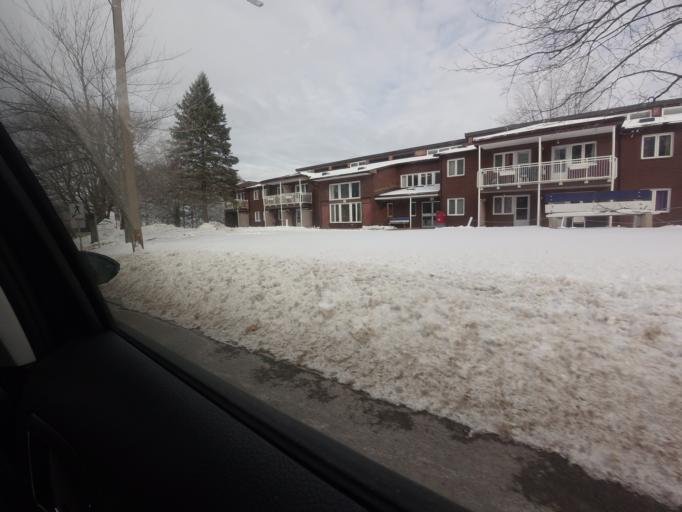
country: CA
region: New Brunswick
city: Oromocto
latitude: 45.8484
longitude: -66.4714
